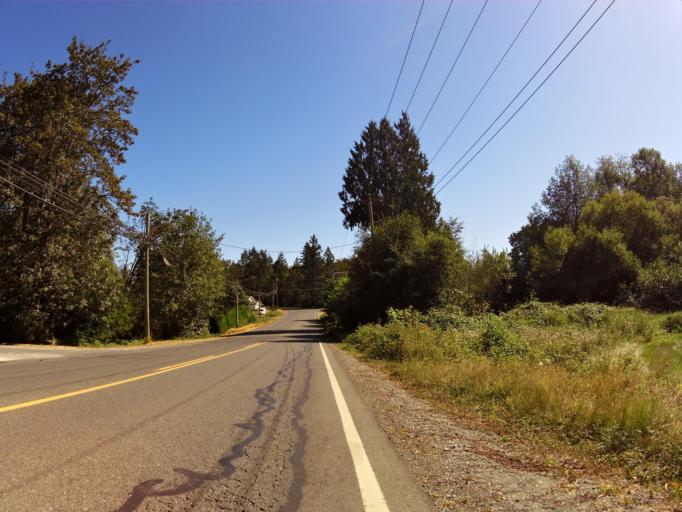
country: CA
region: British Columbia
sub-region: Cowichan Valley Regional District
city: Ladysmith
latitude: 48.9459
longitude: -123.7606
